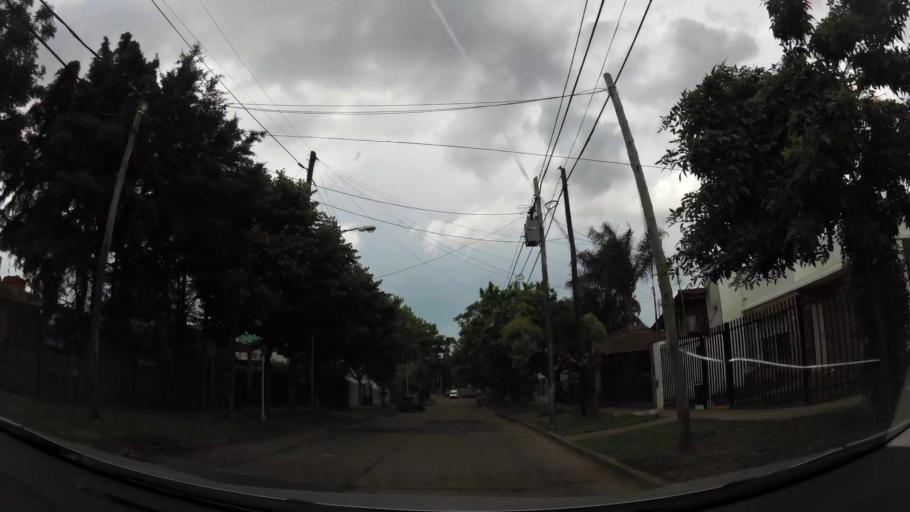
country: AR
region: Buenos Aires
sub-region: Partido de Tigre
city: Tigre
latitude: -34.4647
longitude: -58.6480
